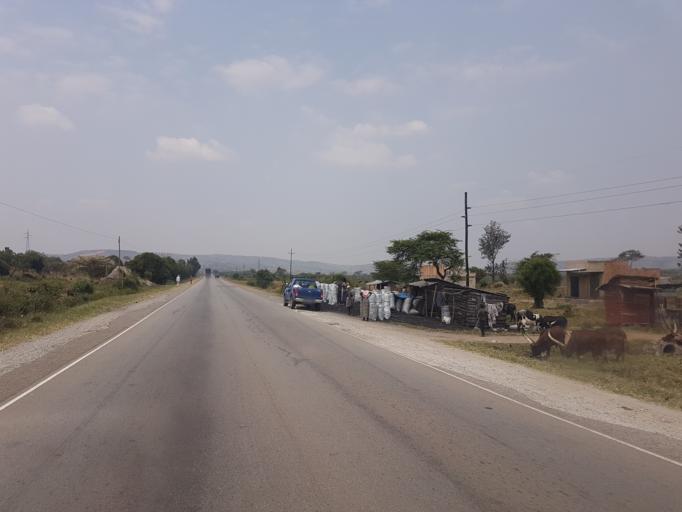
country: UG
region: Western Region
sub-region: Mbarara District
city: Mbarara
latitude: -0.5106
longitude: 30.8216
